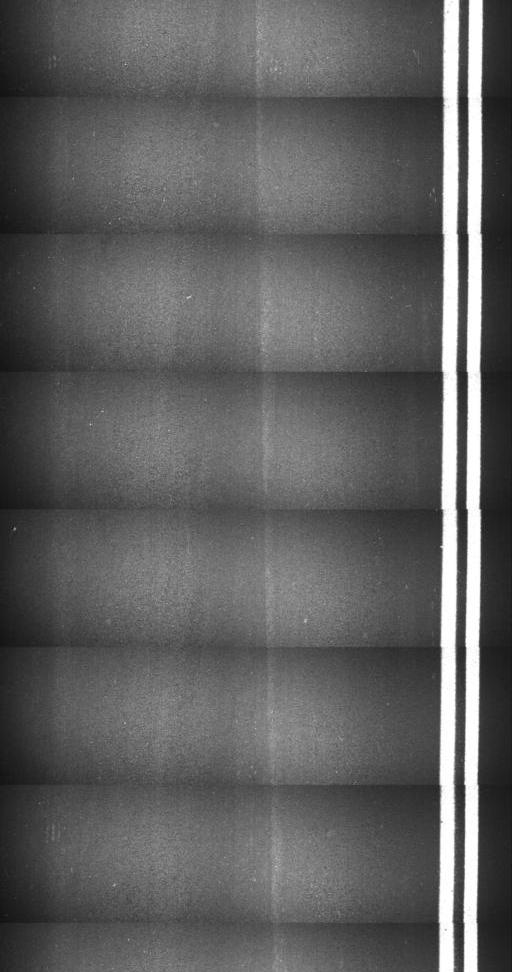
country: US
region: Vermont
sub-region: Windsor County
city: Woodstock
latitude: 43.5747
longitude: -72.5156
